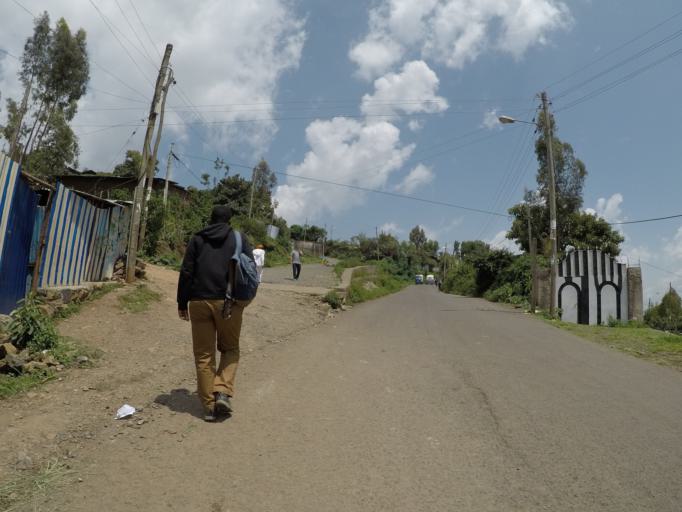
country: ET
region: Amhara
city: Gondar
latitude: 12.6143
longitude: 37.4772
